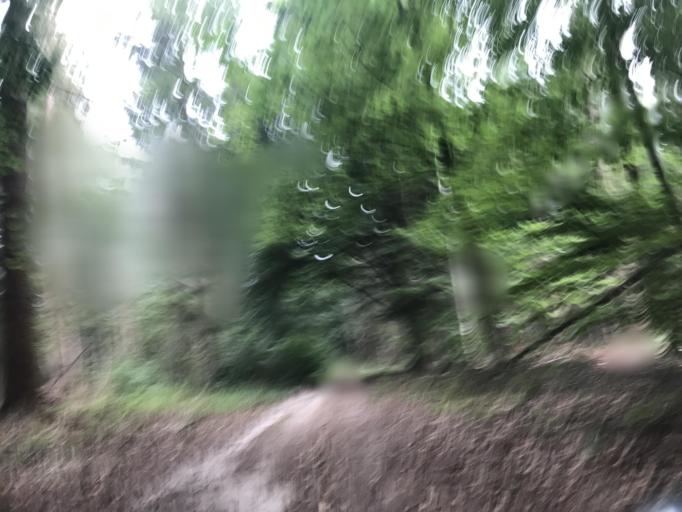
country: DE
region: Lower Saxony
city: Barendorf
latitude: 53.2176
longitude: 10.5362
